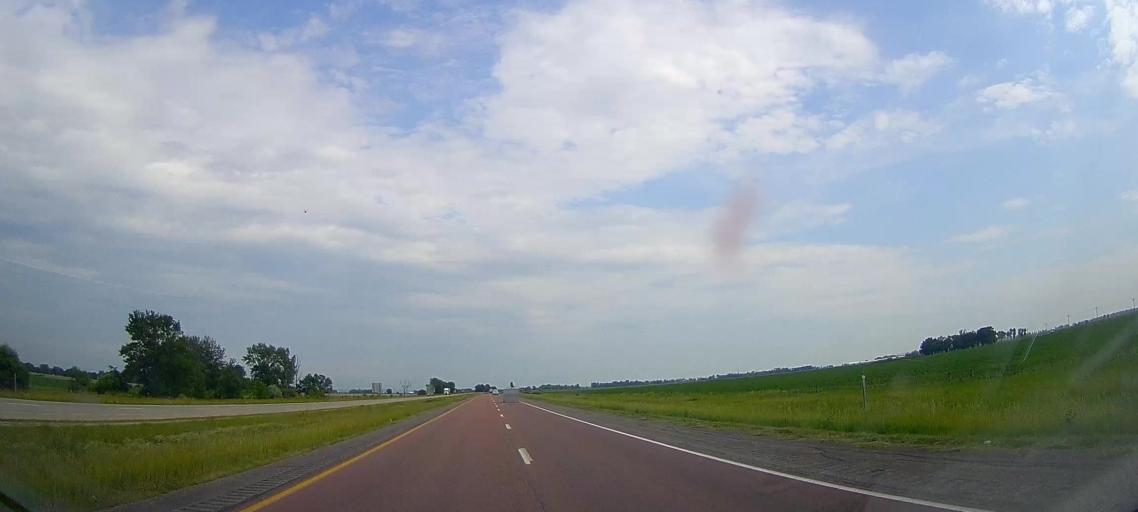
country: US
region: Iowa
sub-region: Monona County
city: Onawa
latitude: 42.0171
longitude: -96.1244
